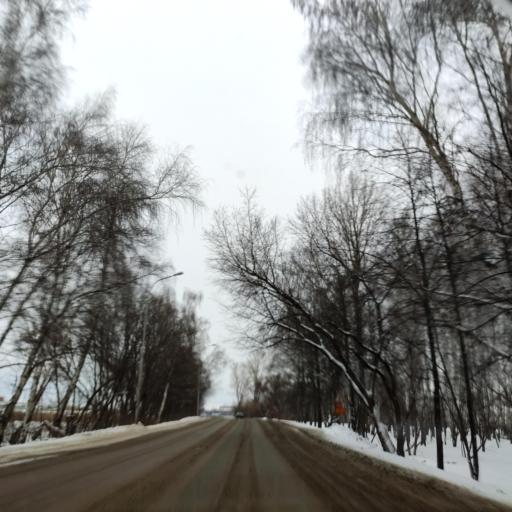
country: RU
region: Bashkortostan
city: Avdon
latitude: 54.7191
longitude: 55.8088
